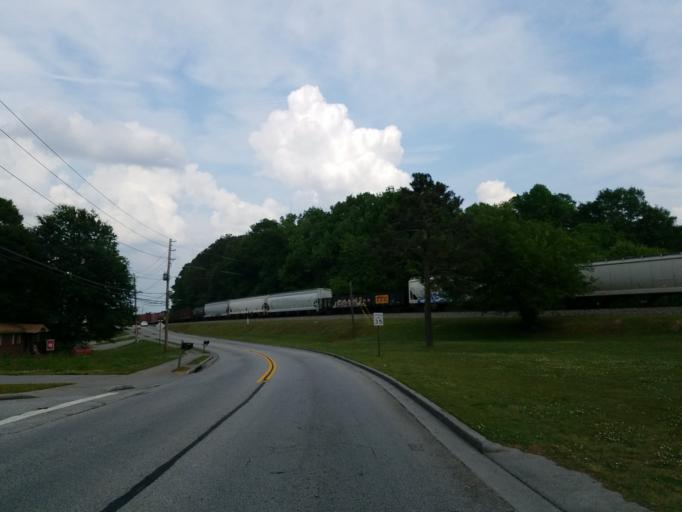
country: US
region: Georgia
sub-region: Cobb County
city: Austell
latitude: 33.8109
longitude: -84.6414
